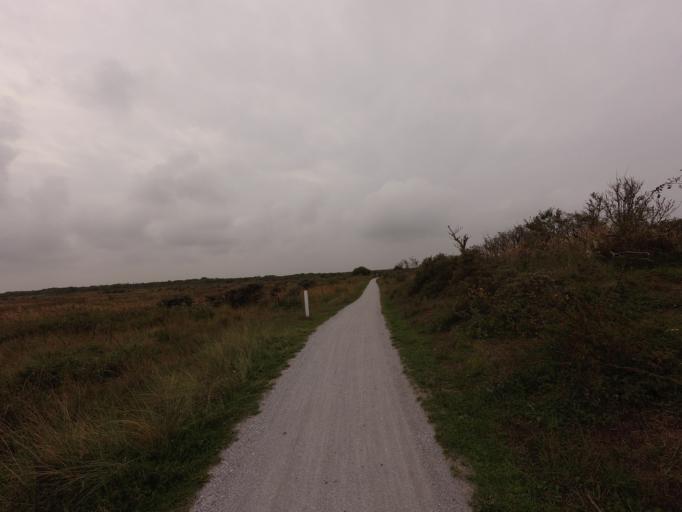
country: NL
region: Friesland
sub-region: Gemeente Schiermonnikoog
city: Schiermonnikoog
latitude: 53.4891
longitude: 6.2048
